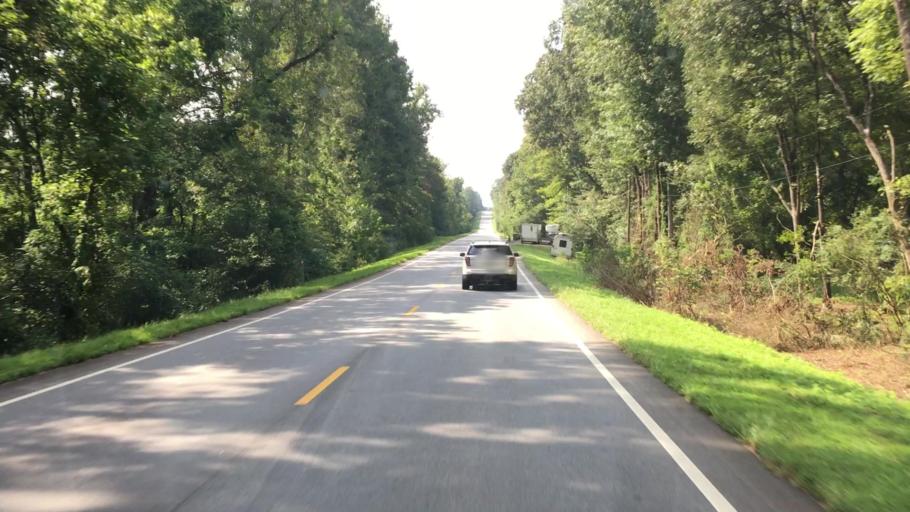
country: US
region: Georgia
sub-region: Jasper County
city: Monticello
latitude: 33.3185
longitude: -83.6950
